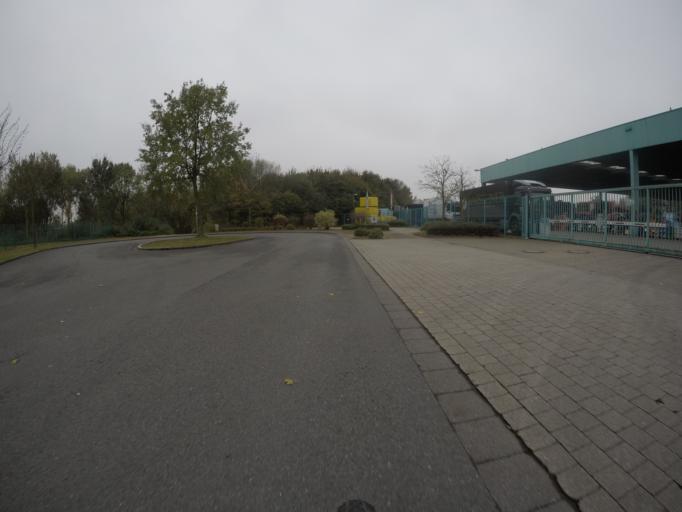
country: DE
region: North Rhine-Westphalia
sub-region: Regierungsbezirk Dusseldorf
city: Bocholt
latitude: 51.8113
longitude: 6.5715
